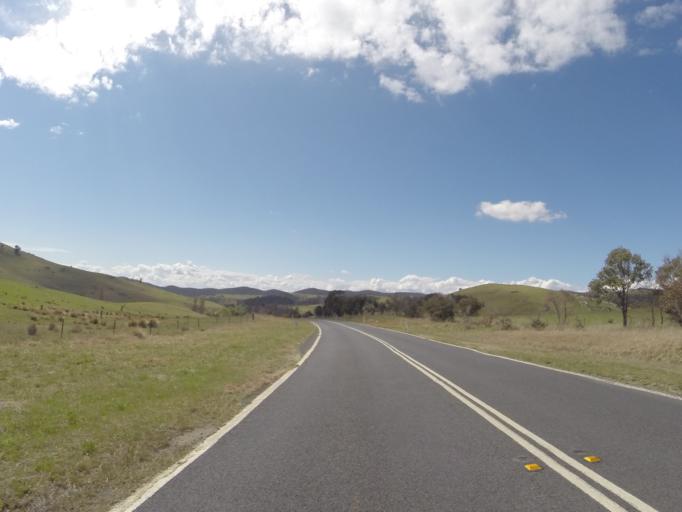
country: AU
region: Australian Capital Territory
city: Macarthur
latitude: -35.4061
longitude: 148.9552
